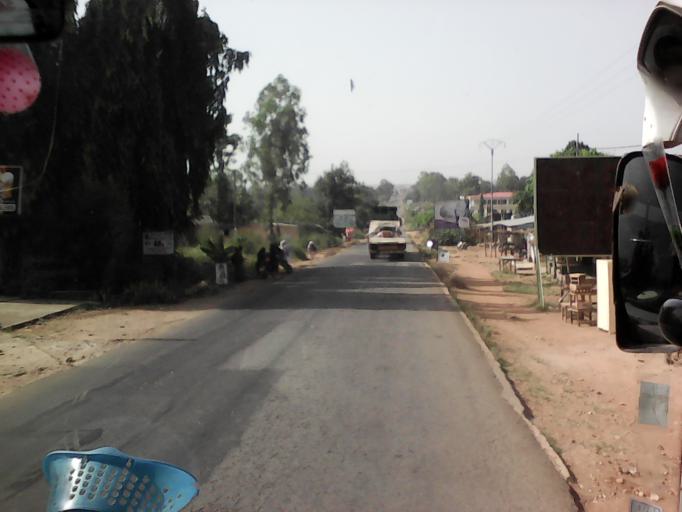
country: TG
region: Centrale
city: Sokode
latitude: 9.0160
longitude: 1.1390
